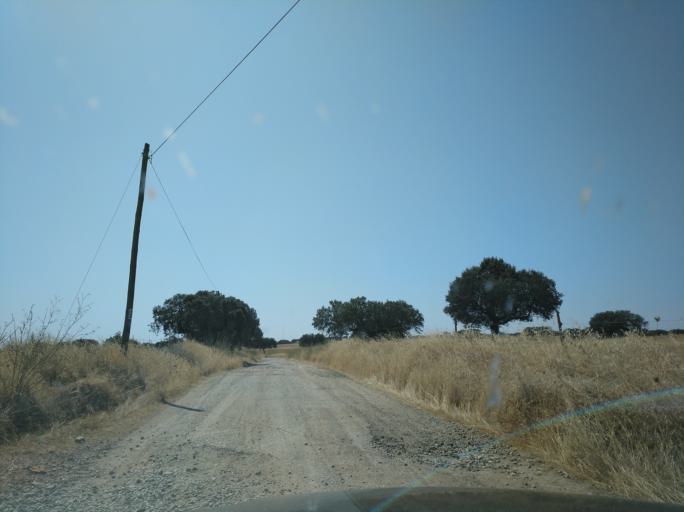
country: PT
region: Portalegre
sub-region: Campo Maior
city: Campo Maior
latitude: 39.0340
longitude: -6.9837
